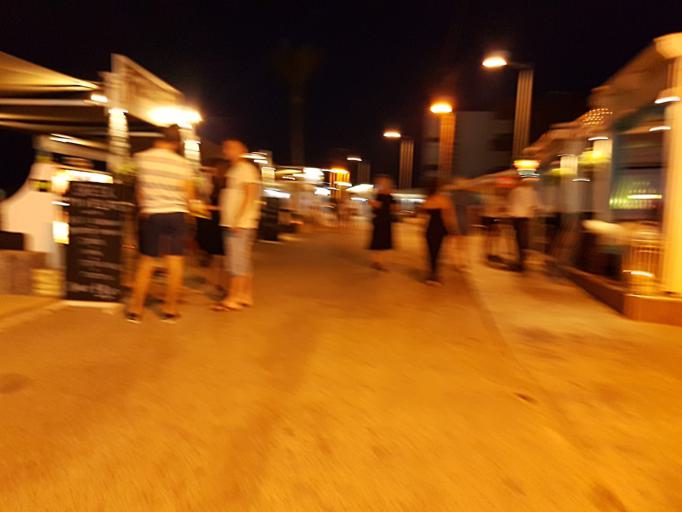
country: GR
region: Crete
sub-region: Nomos Irakleiou
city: Limin Khersonisou
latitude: 35.3228
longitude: 25.3906
